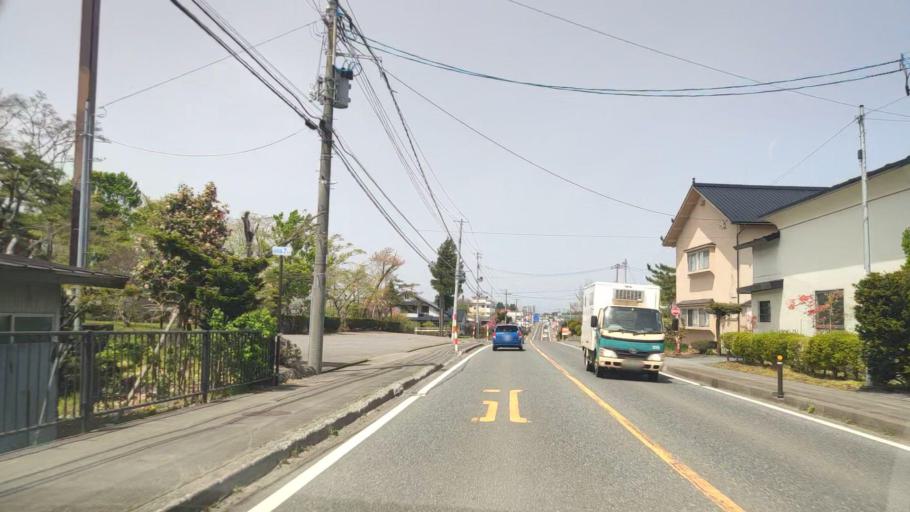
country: JP
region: Aomori
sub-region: Misawa Shi
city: Inuotose
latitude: 40.6536
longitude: 141.1943
